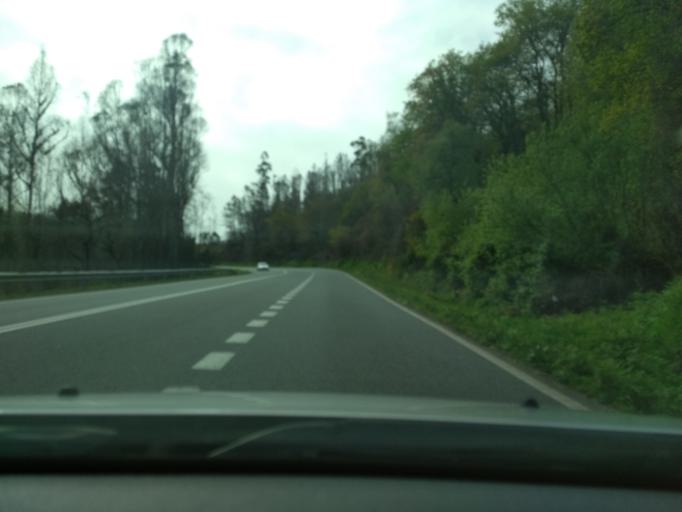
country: ES
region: Galicia
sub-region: Provincia de Pontevedra
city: Catoira
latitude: 42.6512
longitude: -8.6794
